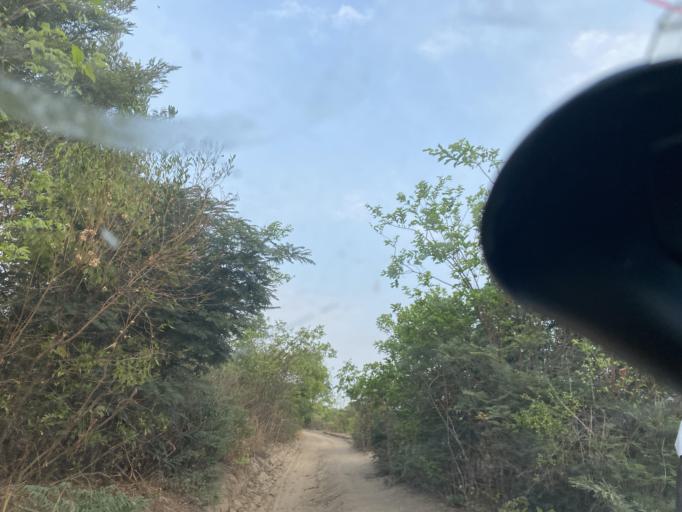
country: ZM
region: Lusaka
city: Chongwe
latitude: -15.2080
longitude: 28.5061
